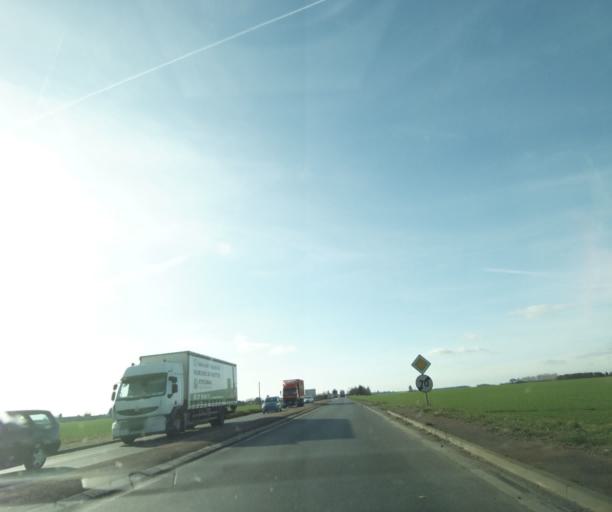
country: FR
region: Ile-de-France
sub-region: Departement de l'Essonne
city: Corbreuse
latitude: 48.4574
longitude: 1.9057
